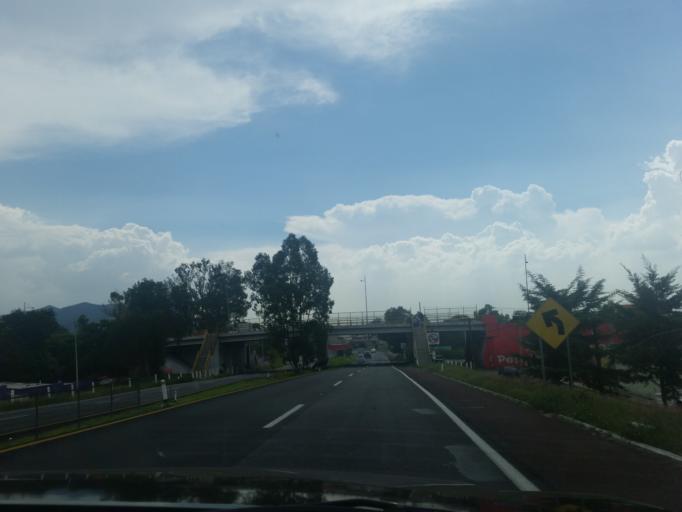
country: MX
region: Mexico
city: Santo Tomas Chiconautla
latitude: 19.6234
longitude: -99.0028
